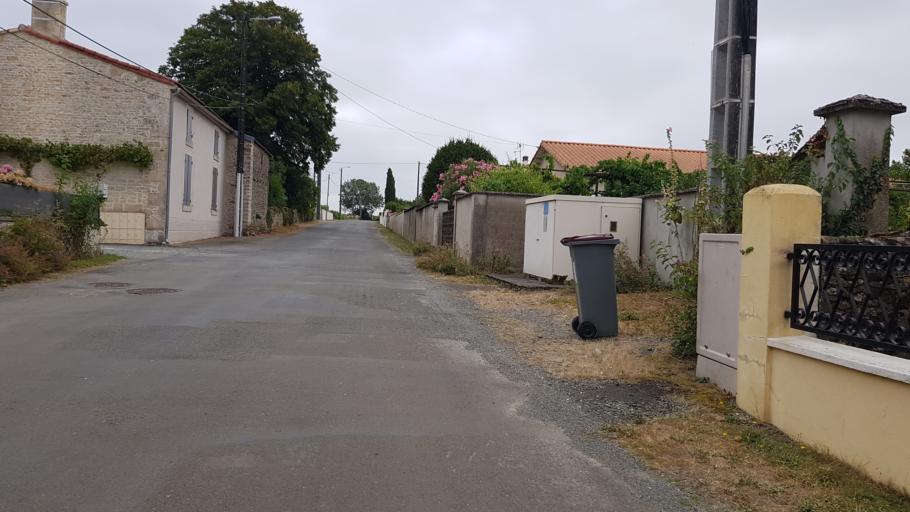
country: FR
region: Poitou-Charentes
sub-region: Departement des Deux-Sevres
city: Vouille
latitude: 46.3237
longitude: -0.3242
